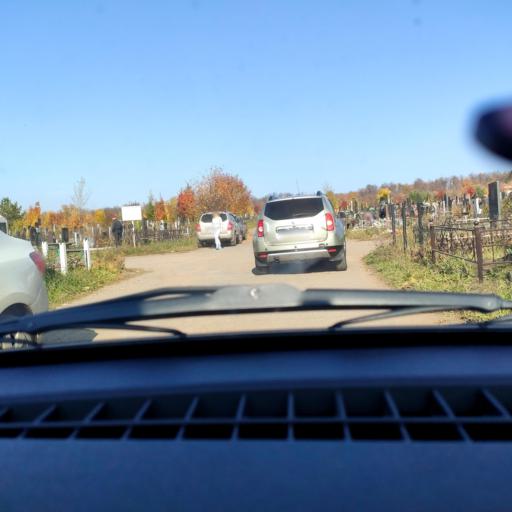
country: RU
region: Bashkortostan
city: Mikhaylovka
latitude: 54.8155
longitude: 55.8665
